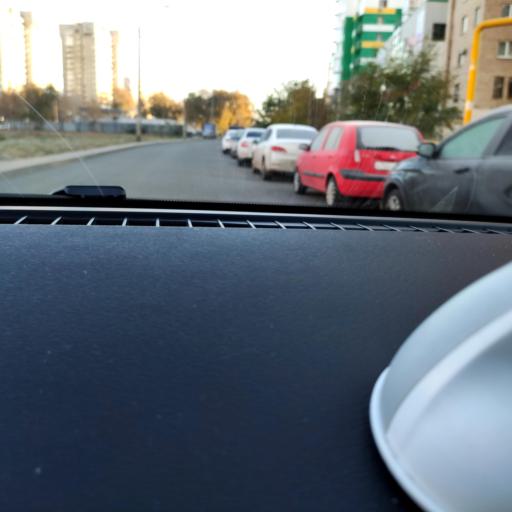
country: RU
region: Samara
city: Samara
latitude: 53.1919
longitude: 50.1379
